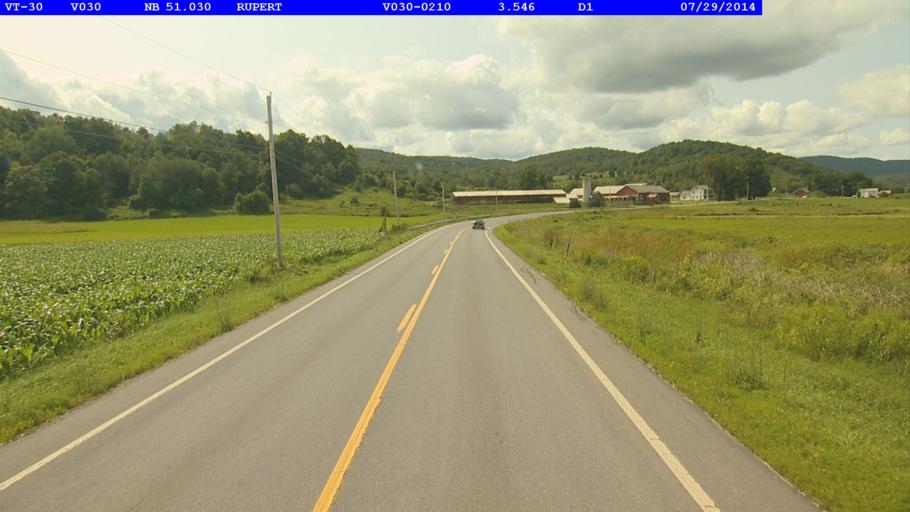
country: US
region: New York
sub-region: Washington County
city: Granville
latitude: 43.3083
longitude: -73.1653
